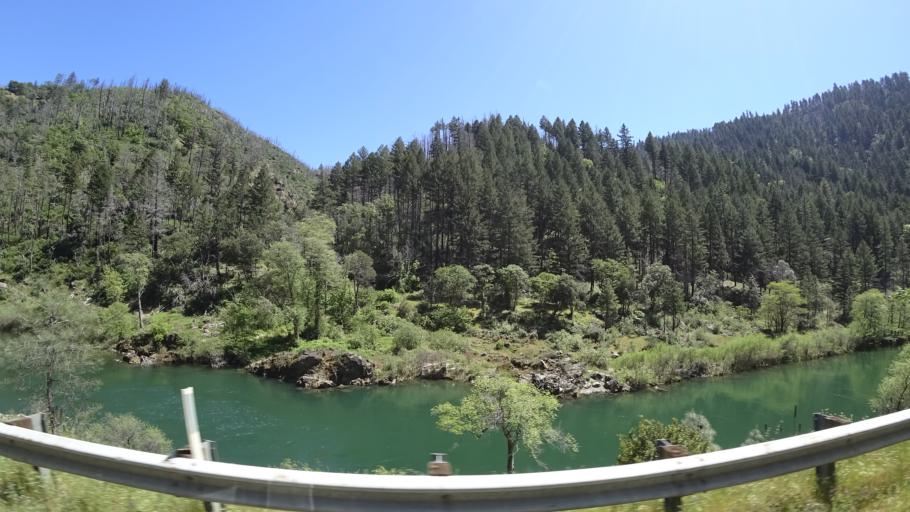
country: US
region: California
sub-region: Humboldt County
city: Willow Creek
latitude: 40.7847
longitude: -123.4197
